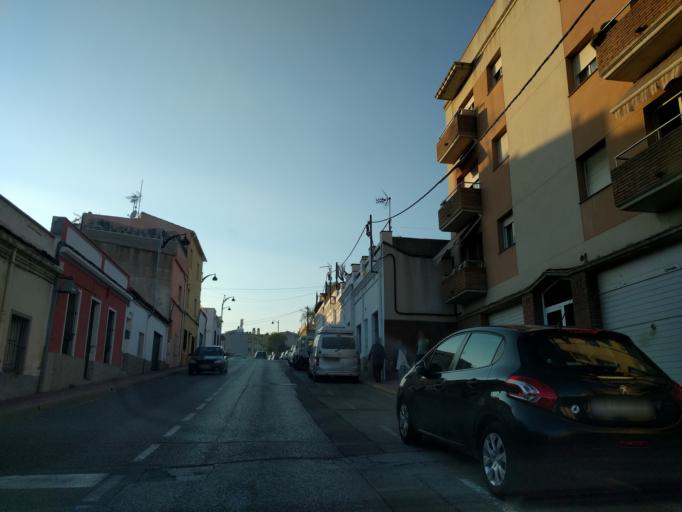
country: ES
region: Catalonia
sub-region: Provincia de Girona
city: Sant Feliu de Guixols
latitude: 41.7880
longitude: 3.0272
